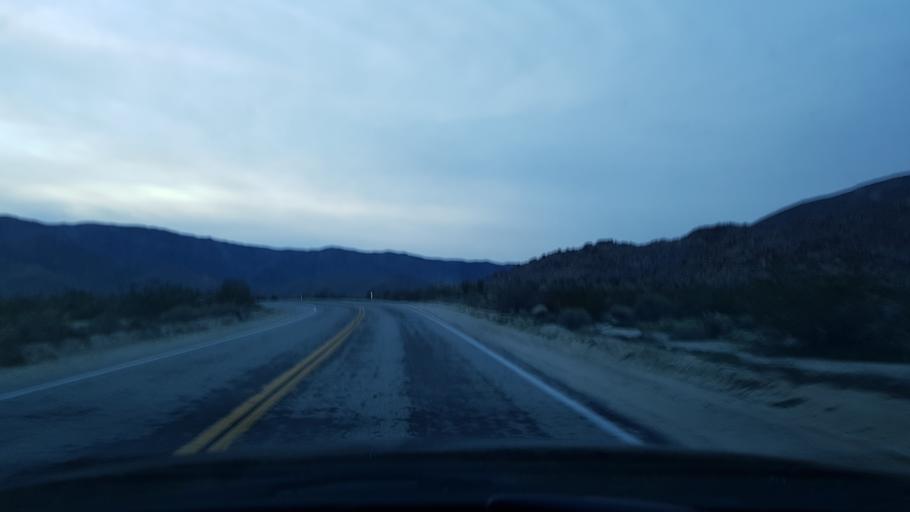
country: US
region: California
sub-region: San Diego County
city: Pine Valley
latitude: 32.9760
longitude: -116.3759
